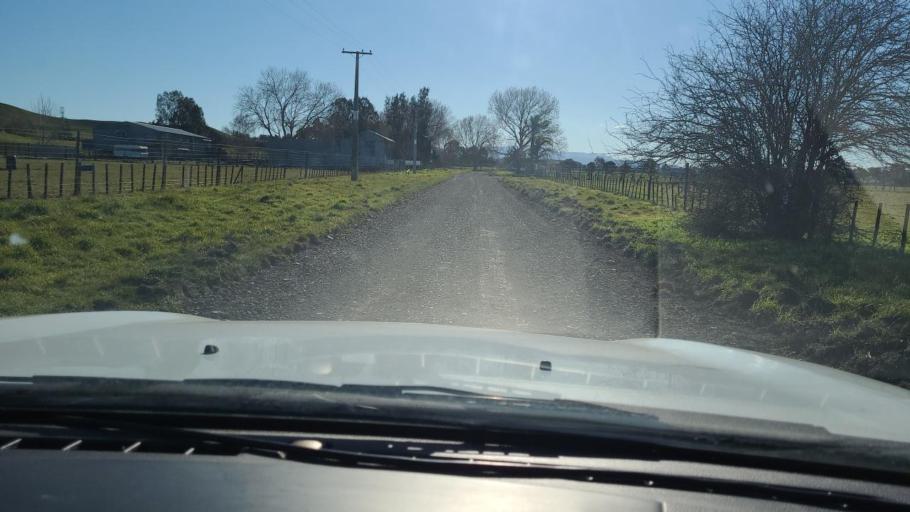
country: NZ
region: Hawke's Bay
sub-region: Napier City
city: Taradale
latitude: -39.4619
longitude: 176.6379
